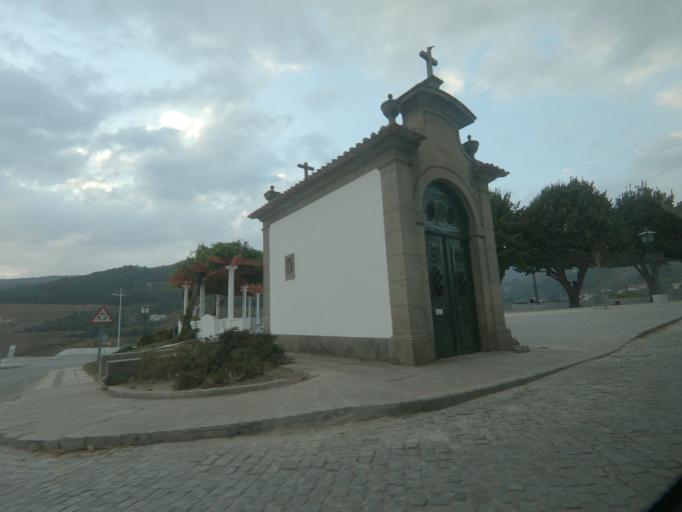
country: PT
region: Vila Real
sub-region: Mesao Frio
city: Mesao Frio
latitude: 41.1587
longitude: -7.8920
